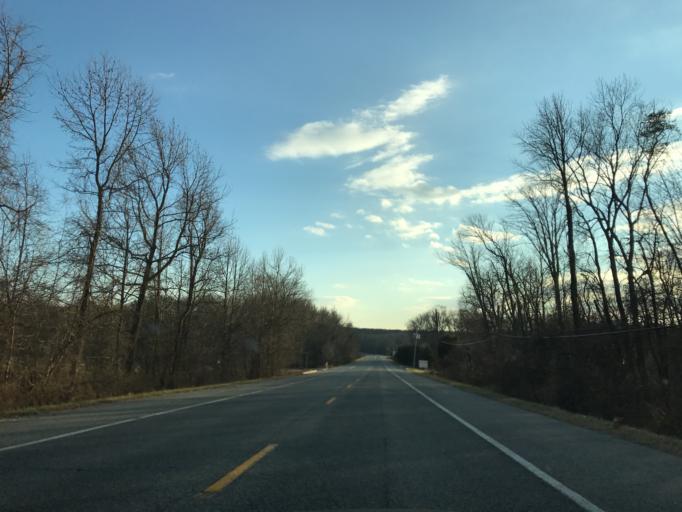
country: US
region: Maryland
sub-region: Cecil County
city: Charlestown
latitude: 39.5643
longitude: -75.9482
